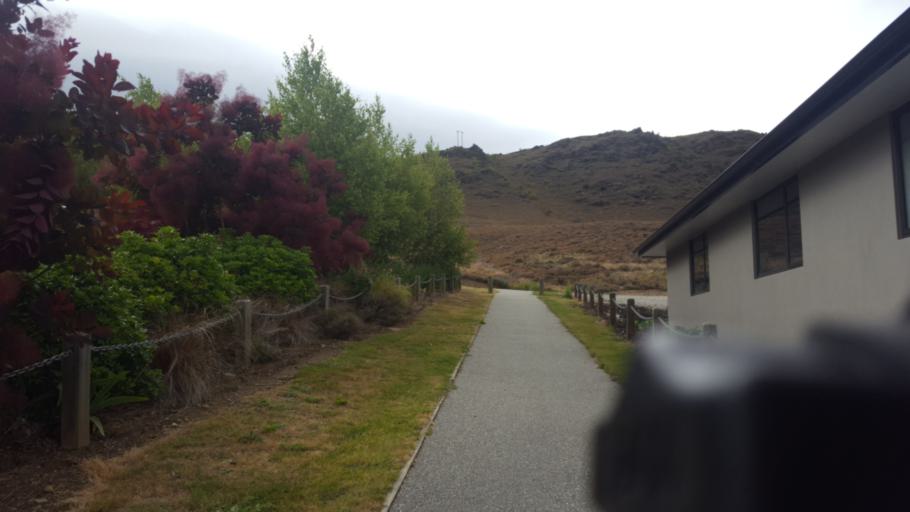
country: NZ
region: Otago
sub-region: Queenstown-Lakes District
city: Wanaka
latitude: -45.2532
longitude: 169.4024
